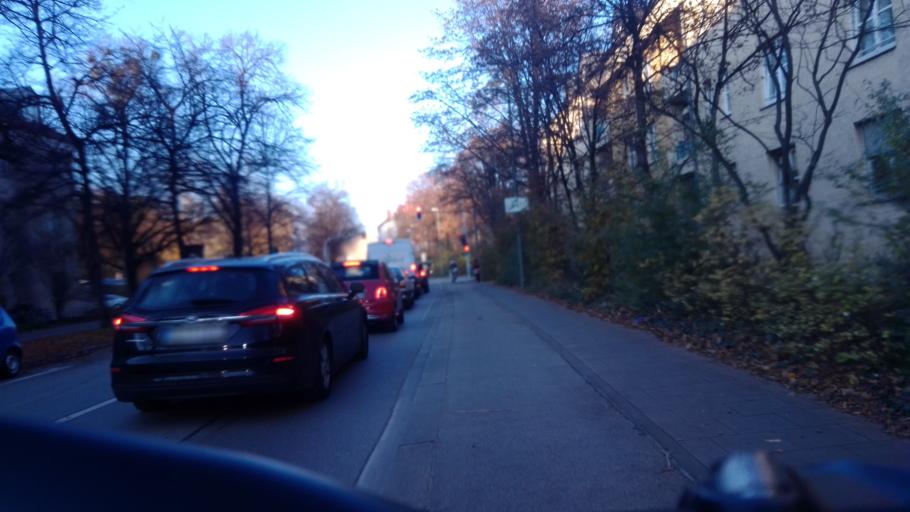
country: DE
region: Bavaria
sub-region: Upper Bavaria
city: Pullach im Isartal
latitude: 48.1084
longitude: 11.5342
